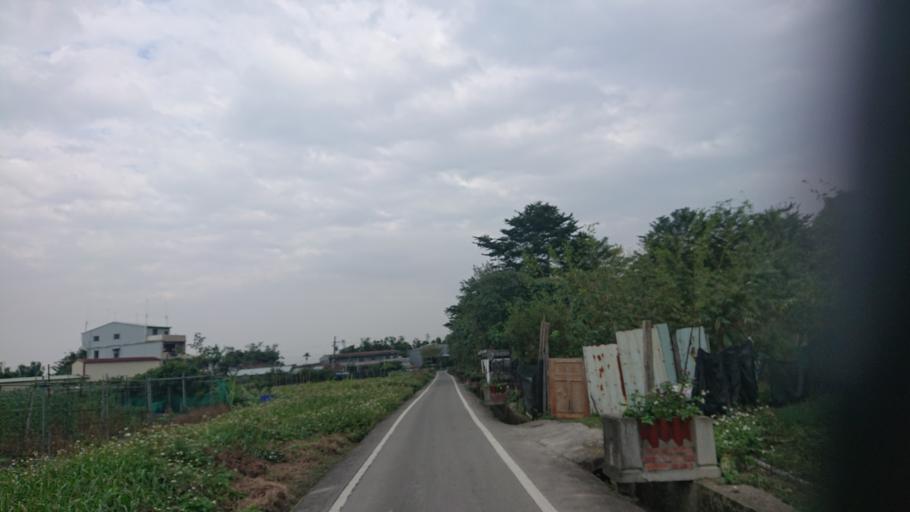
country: TW
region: Taiwan
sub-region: Taoyuan
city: Taoyuan
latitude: 24.9531
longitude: 121.3707
